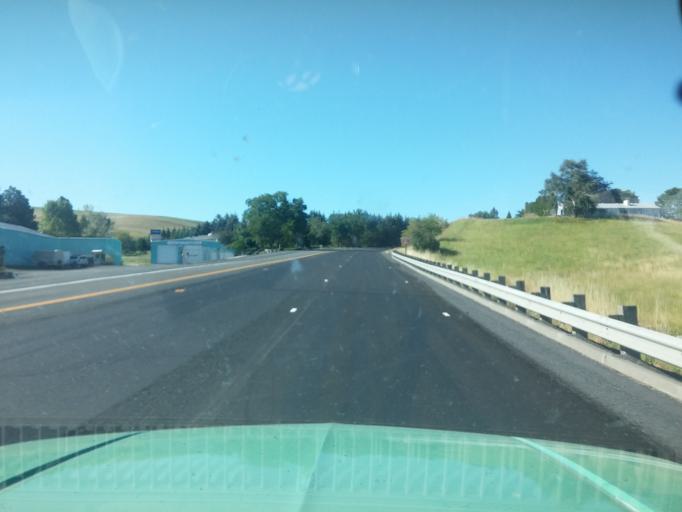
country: US
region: Idaho
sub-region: Latah County
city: Moscow
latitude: 46.6967
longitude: -117.0079
